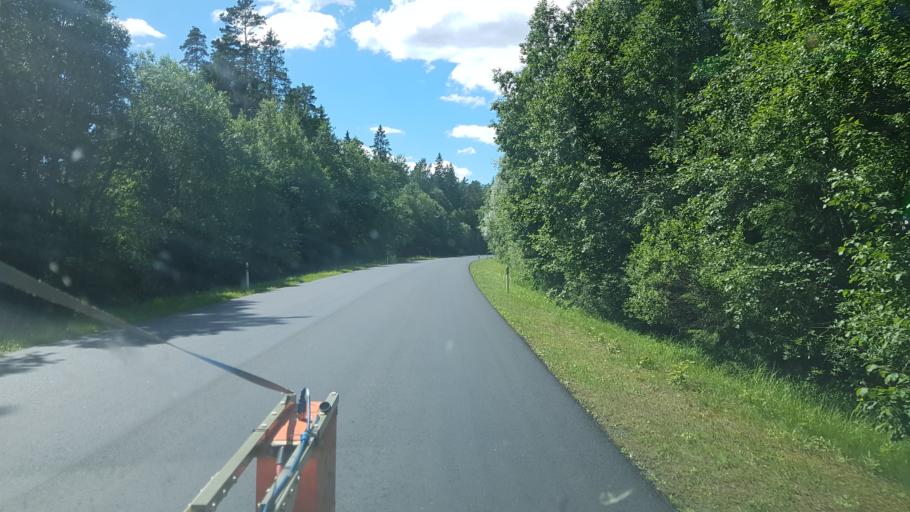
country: EE
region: Viljandimaa
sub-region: Moisakuela linn
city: Moisakula
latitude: 58.2524
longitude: 25.1953
